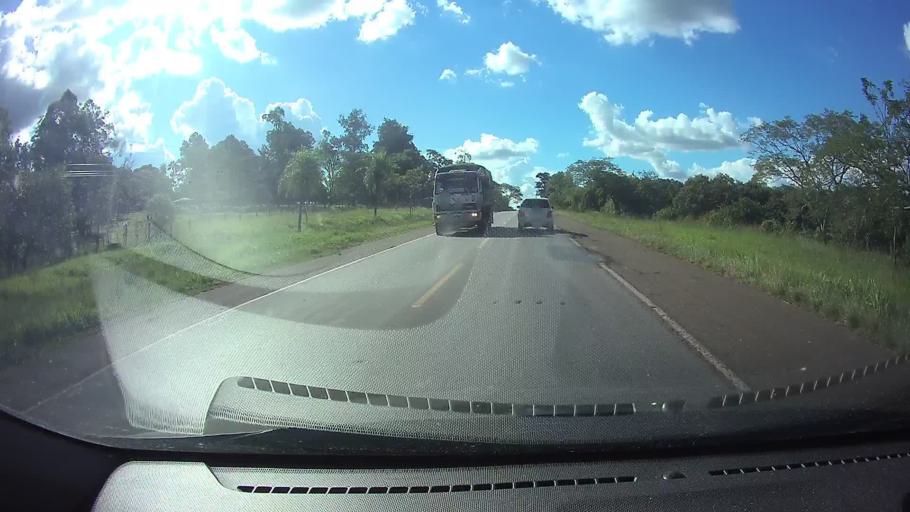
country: PY
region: Cordillera
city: Eusebio Ayala
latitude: -25.4190
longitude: -56.9275
